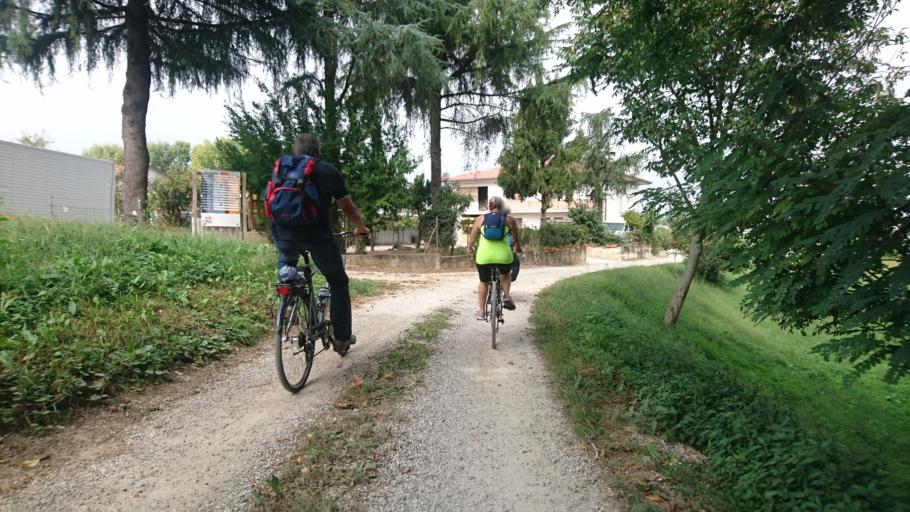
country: IT
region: Veneto
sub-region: Provincia di Padova
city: Grantorto
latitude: 45.5833
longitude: 11.7509
